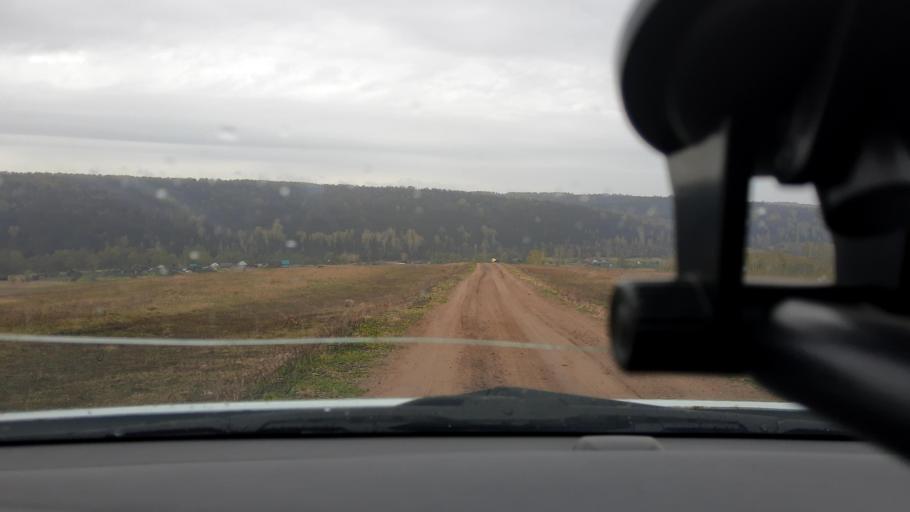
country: RU
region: Bashkortostan
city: Pavlovka
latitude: 55.4323
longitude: 56.3177
